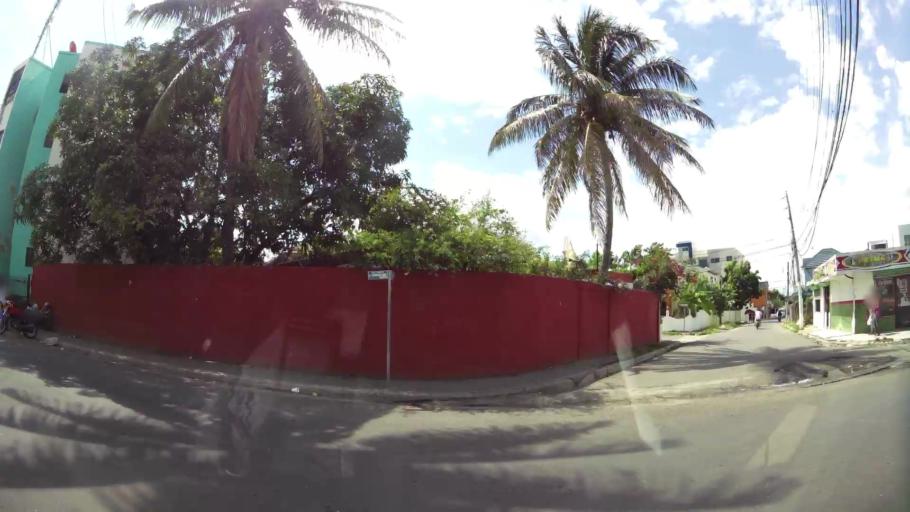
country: DO
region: Santiago
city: Santiago de los Caballeros
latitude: 19.4728
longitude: -70.6986
